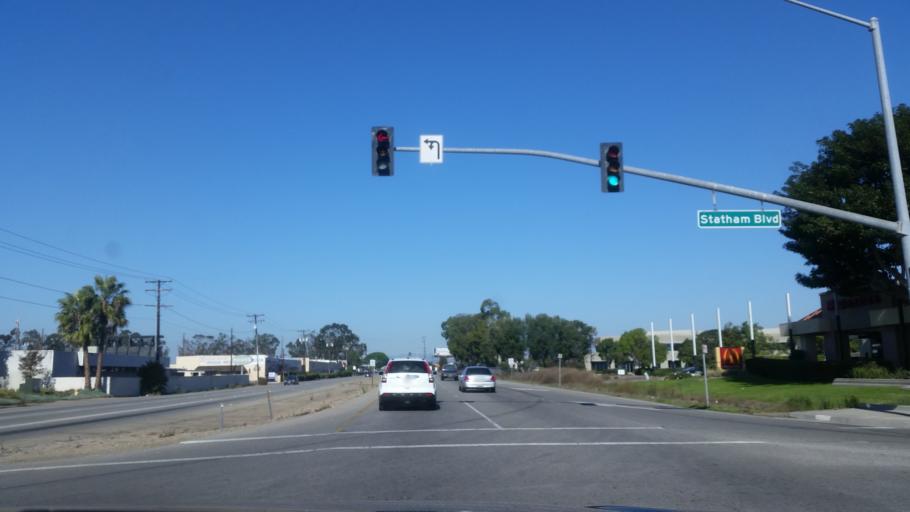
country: US
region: California
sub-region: Ventura County
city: Oxnard
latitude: 34.1799
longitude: -119.1650
